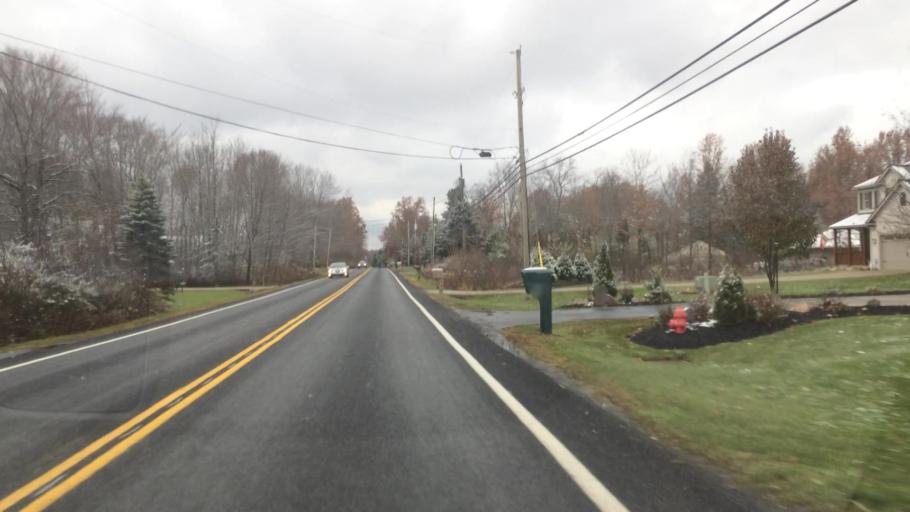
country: US
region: Ohio
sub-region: Summit County
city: Boston Heights
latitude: 41.2871
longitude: -81.5179
